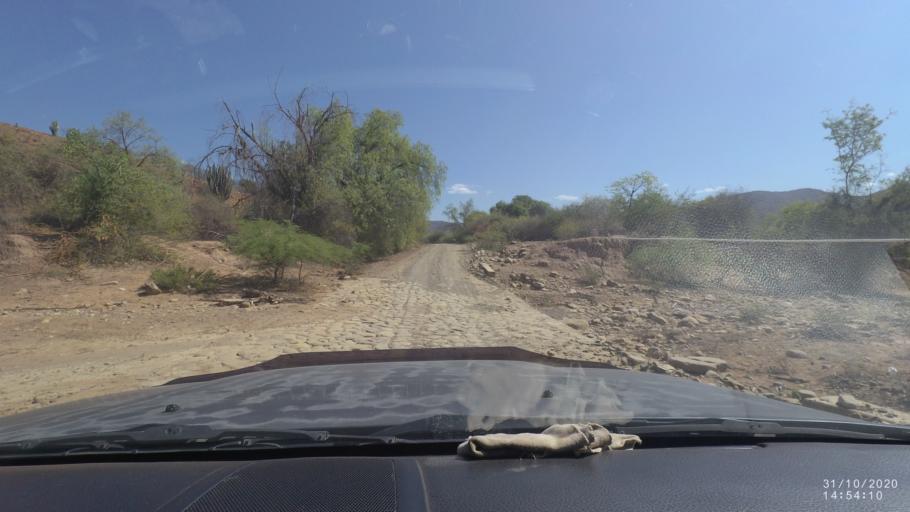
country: BO
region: Cochabamba
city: Aiquile
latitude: -18.2241
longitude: -64.8572
